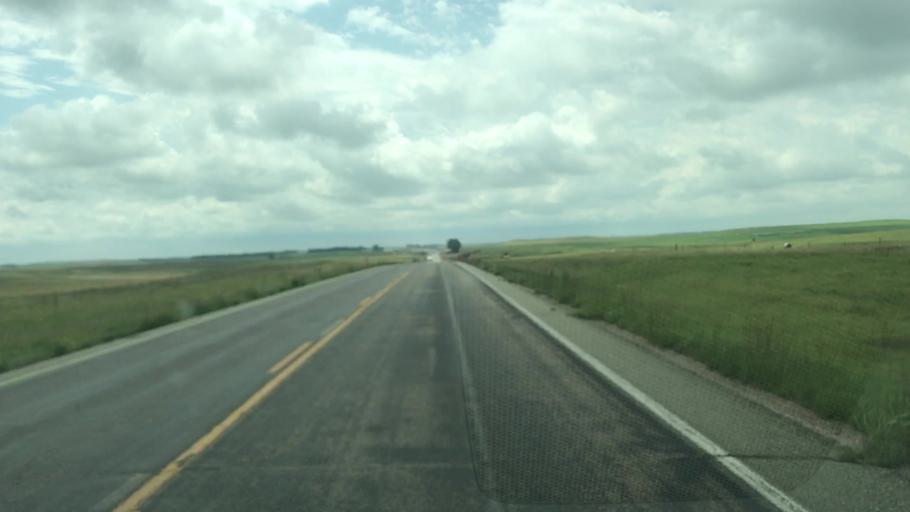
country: US
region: Nebraska
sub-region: Cherry County
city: Valentine
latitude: 43.0581
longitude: -100.5949
